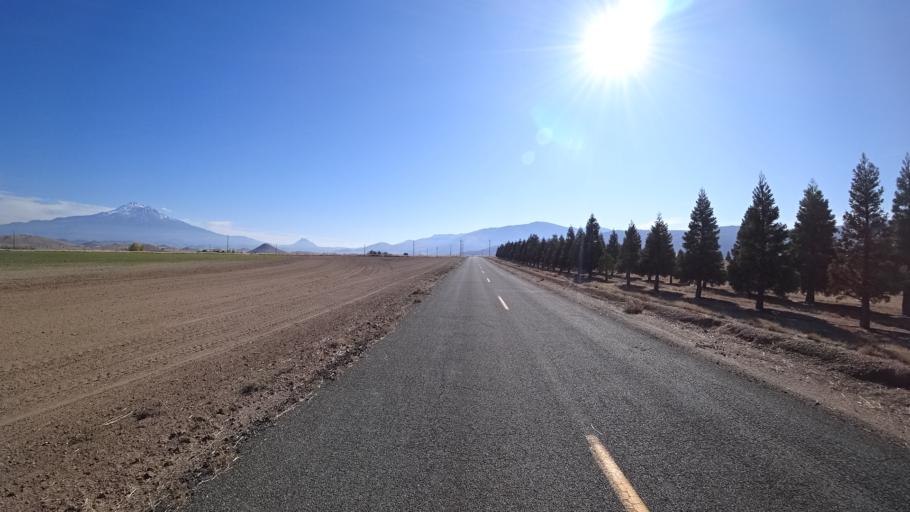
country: US
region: California
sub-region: Siskiyou County
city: Montague
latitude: 41.5534
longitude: -122.5451
